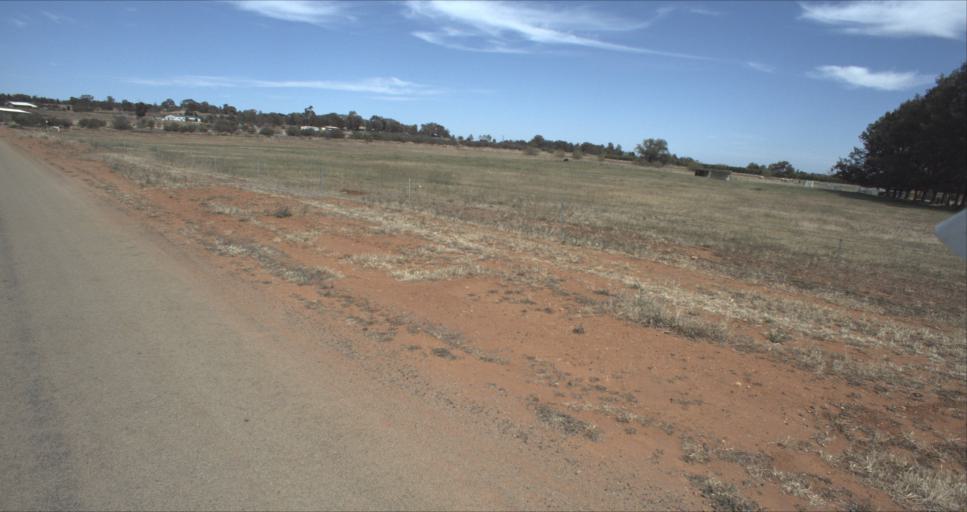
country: AU
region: New South Wales
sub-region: Leeton
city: Leeton
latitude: -34.5716
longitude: 146.4556
